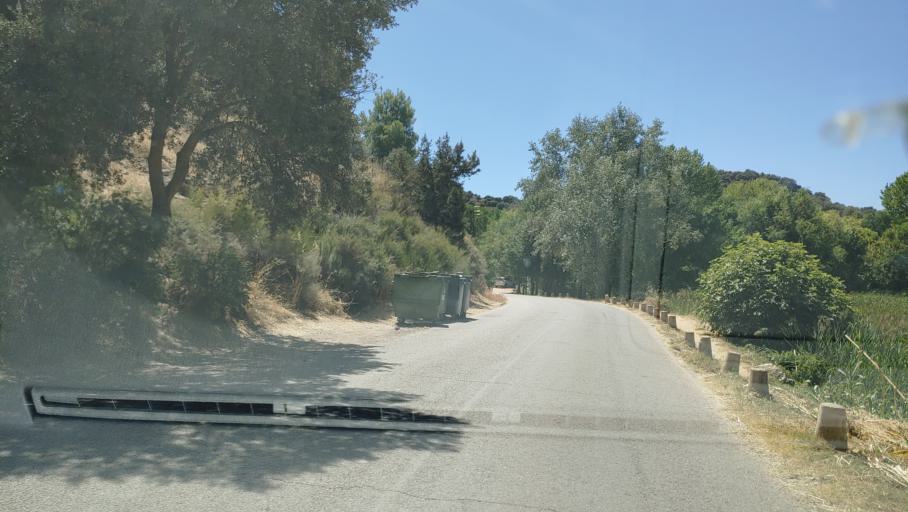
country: ES
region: Castille-La Mancha
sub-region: Provincia de Ciudad Real
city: Ruidera
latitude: 38.9388
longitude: -2.8471
